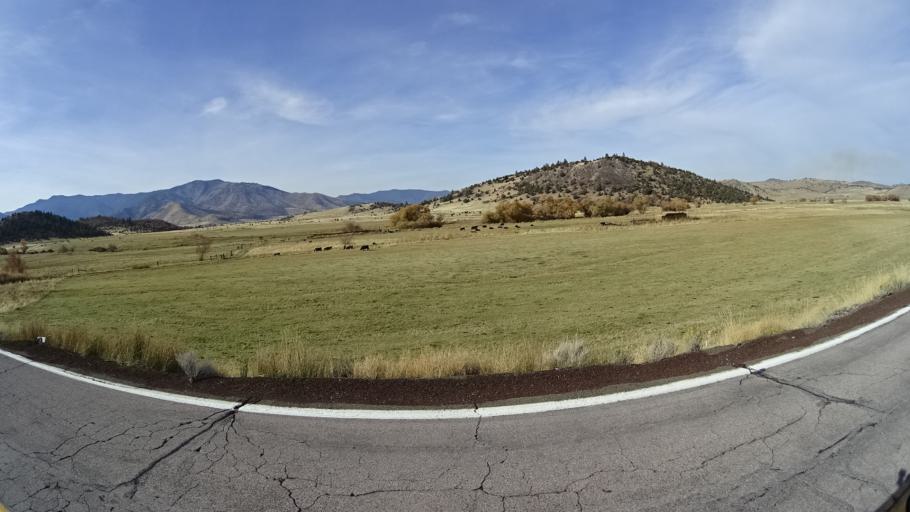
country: US
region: California
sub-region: Siskiyou County
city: Weed
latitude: 41.4769
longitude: -122.4113
